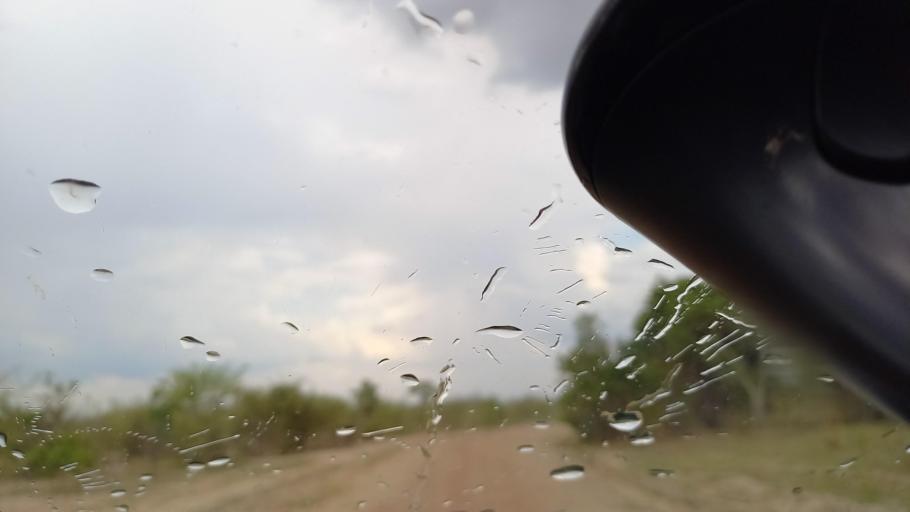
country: ZM
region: Lusaka
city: Kafue
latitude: -15.8549
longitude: 28.1167
